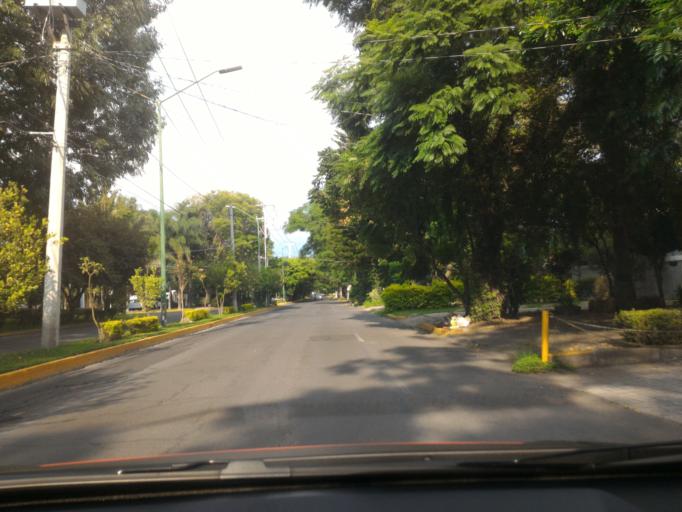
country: MX
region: Jalisco
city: Guadalajara
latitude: 20.6597
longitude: -103.3953
